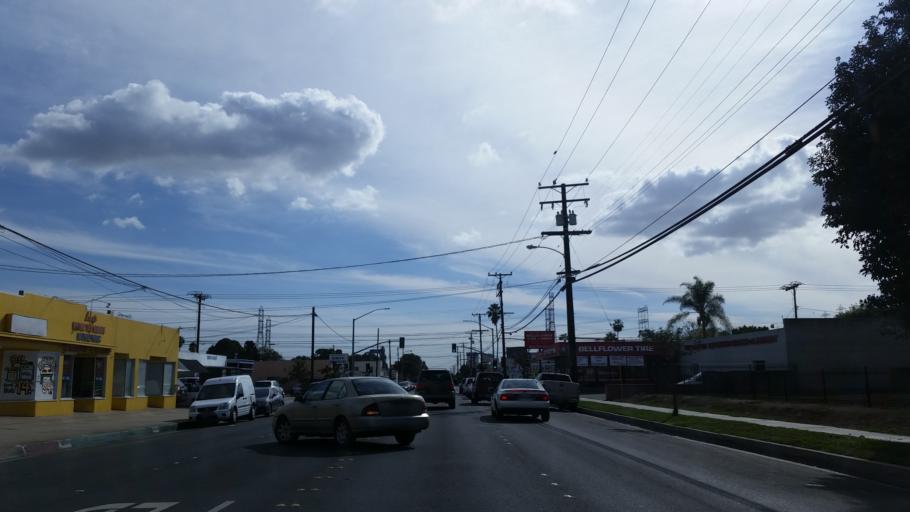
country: US
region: California
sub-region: Los Angeles County
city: Lakewood
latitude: 33.8723
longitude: -118.1339
